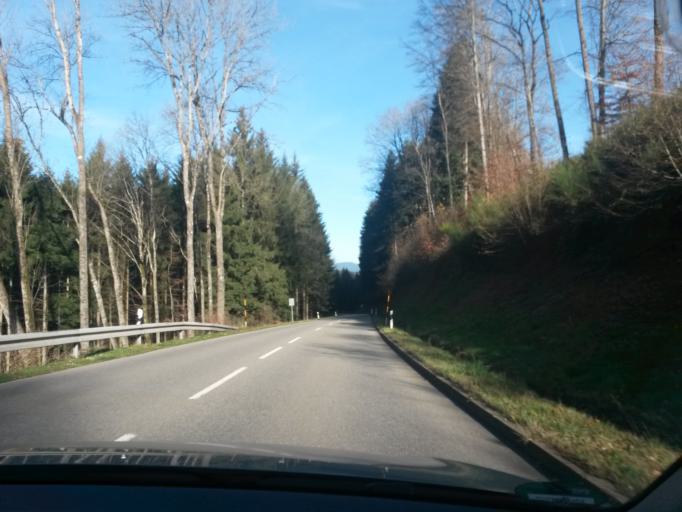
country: DE
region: Baden-Wuerttemberg
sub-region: Freiburg Region
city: Muhlenbach
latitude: 48.2189
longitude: 8.0966
